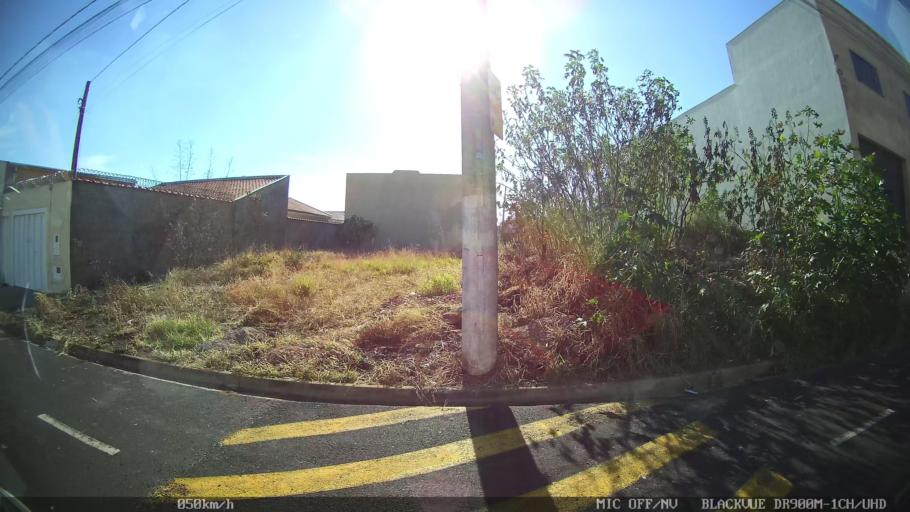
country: BR
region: Sao Paulo
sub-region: Franca
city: Franca
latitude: -20.5135
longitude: -47.4265
